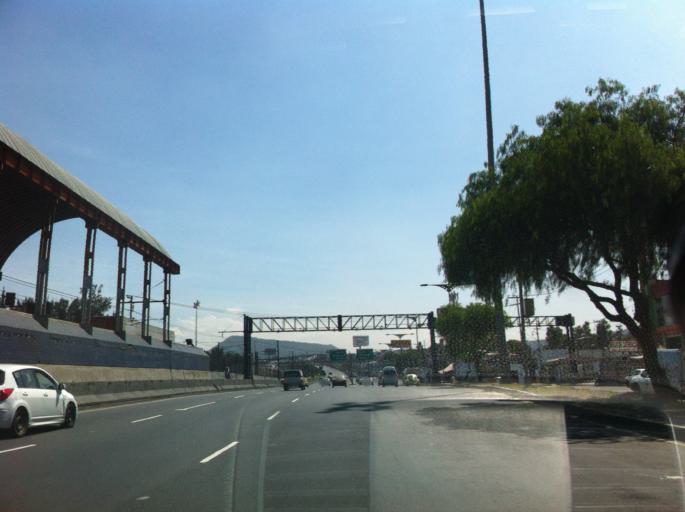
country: MX
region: Mexico
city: Los Reyes La Paz
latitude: 19.3645
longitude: -99.0057
